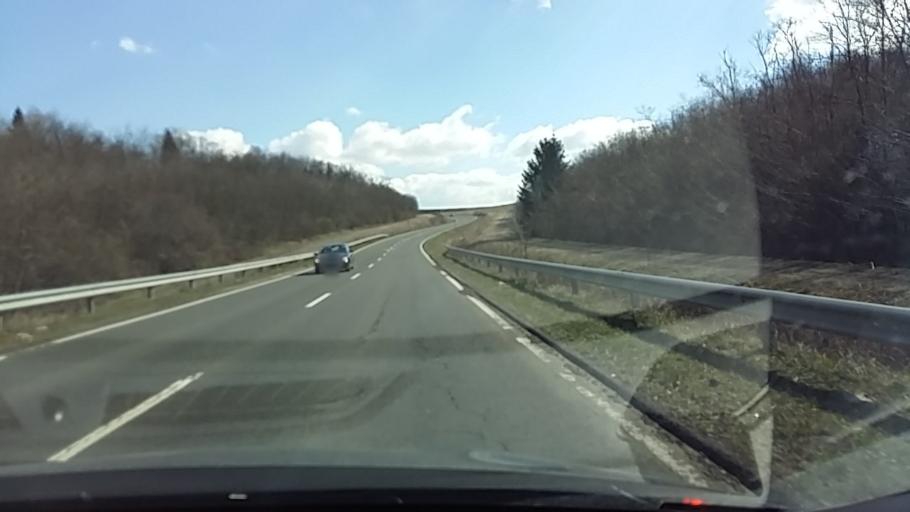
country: HU
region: Baranya
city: Kozarmisleny
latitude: 46.0263
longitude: 18.2791
